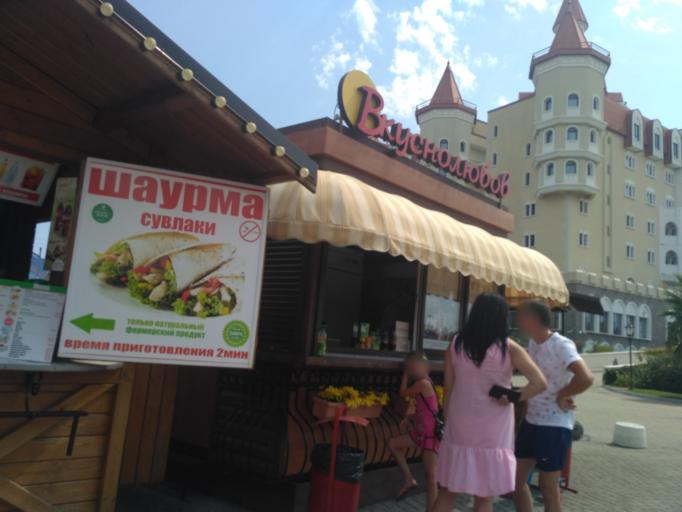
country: RU
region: Krasnodarskiy
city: Adler
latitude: 43.4046
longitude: 39.9634
